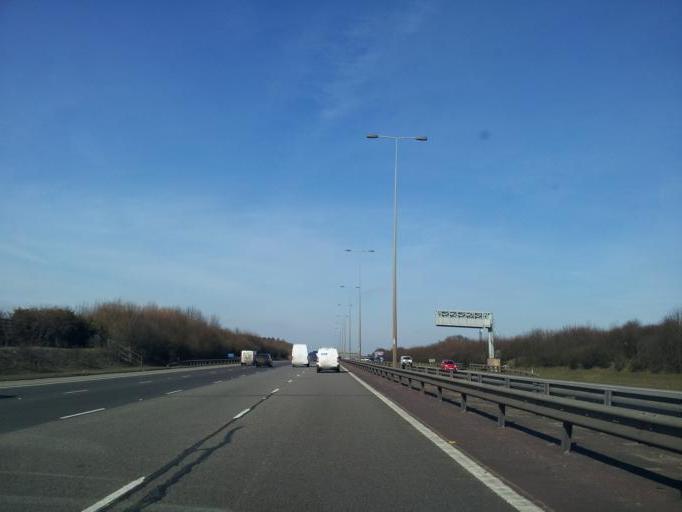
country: GB
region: England
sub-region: Cambridgeshire
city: Sawtry
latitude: 52.3948
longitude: -0.2608
